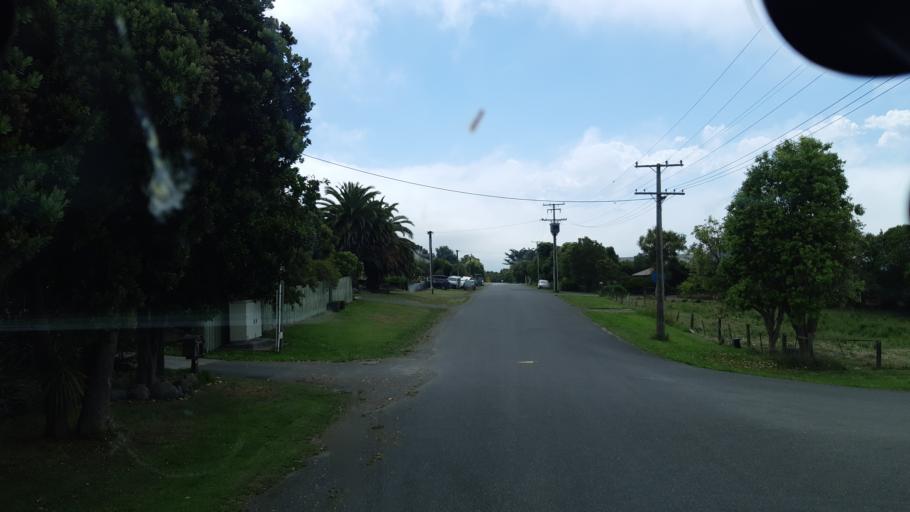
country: NZ
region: Canterbury
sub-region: Kaikoura District
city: Kaikoura
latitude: -42.4193
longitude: 173.6969
